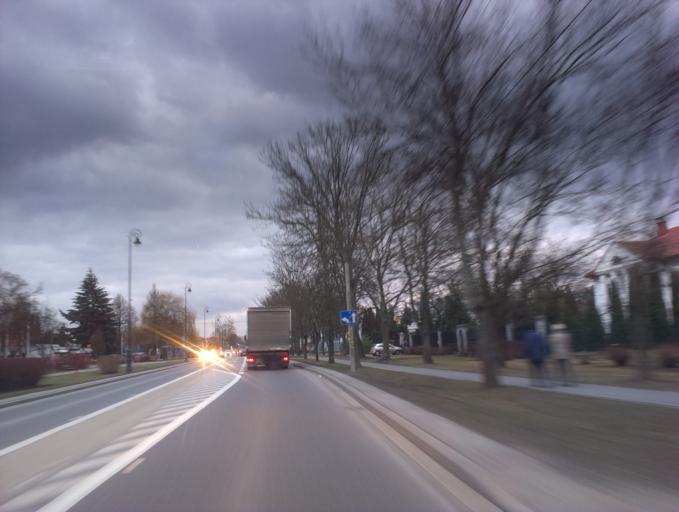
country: PL
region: Masovian Voivodeship
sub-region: Powiat piaseczynski
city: Konstancin-Jeziorna
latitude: 52.0988
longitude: 21.1158
